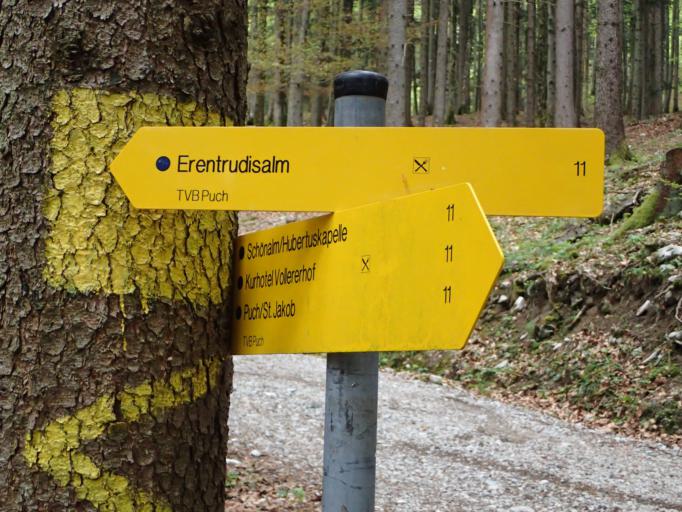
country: AT
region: Salzburg
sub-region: Politischer Bezirk Salzburg-Umgebung
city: Elsbethen
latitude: 47.7429
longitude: 13.1225
